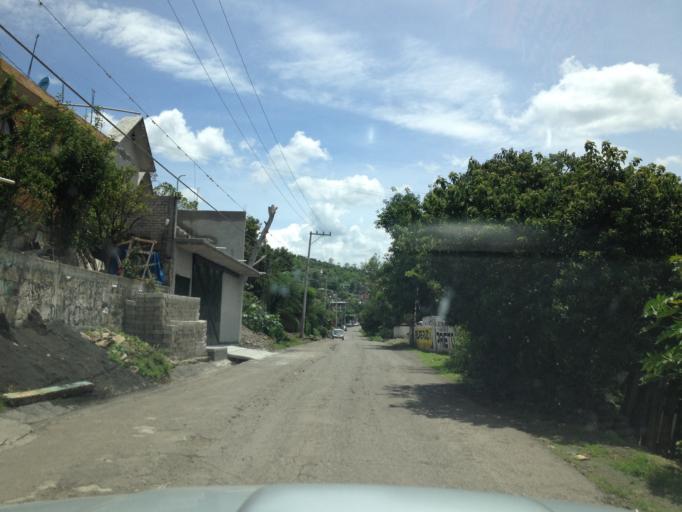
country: MX
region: Michoacan
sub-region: Tarimbaro
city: El Colegio
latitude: 19.7734
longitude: -101.1728
